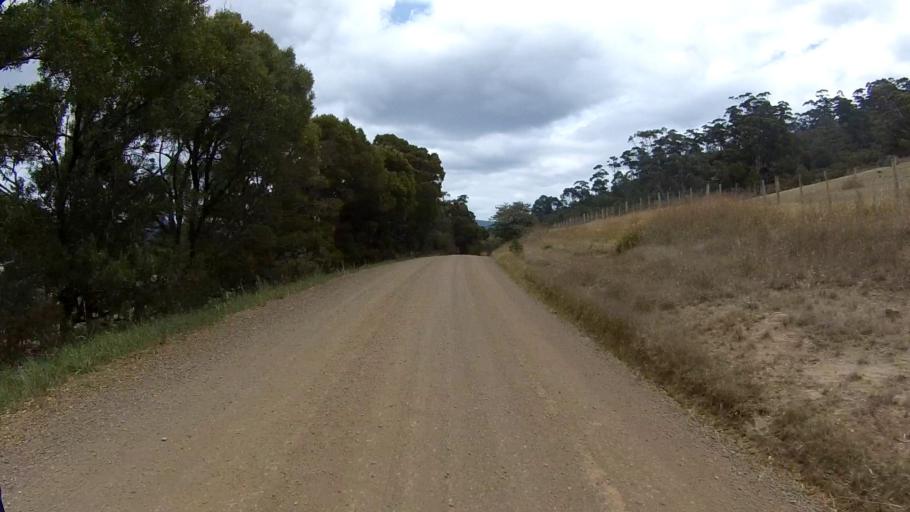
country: AU
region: Tasmania
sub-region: Sorell
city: Sorell
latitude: -42.6278
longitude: 147.9318
